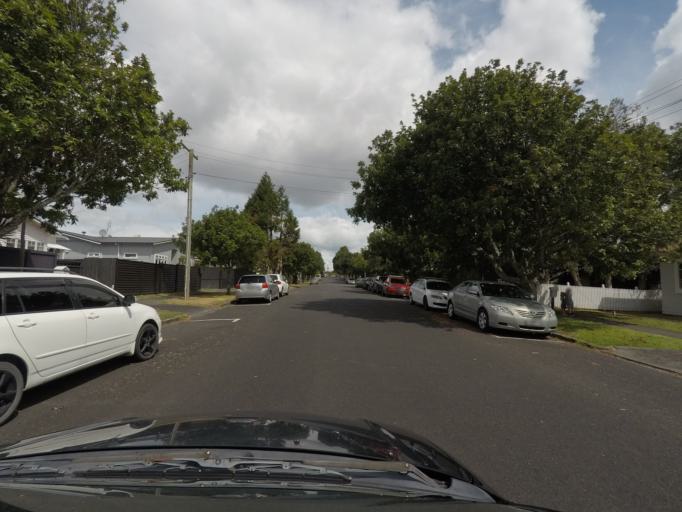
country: NZ
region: Auckland
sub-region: Auckland
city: Rosebank
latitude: -36.8827
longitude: 174.7095
